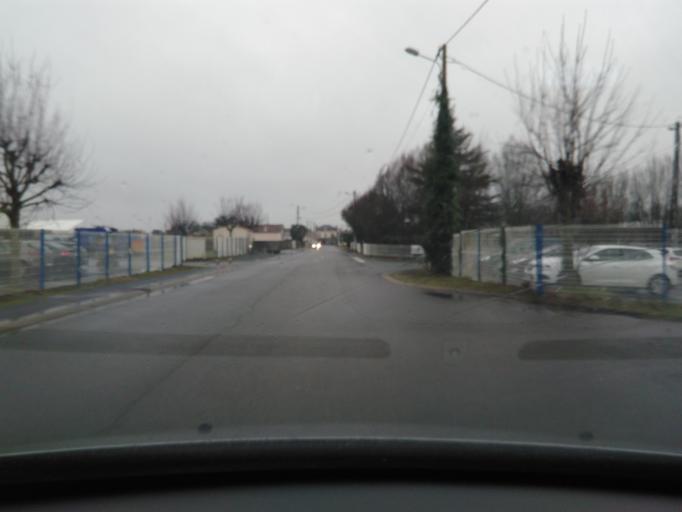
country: FR
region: Pays de la Loire
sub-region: Departement de la Vendee
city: Lucon
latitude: 46.4666
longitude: -1.1670
